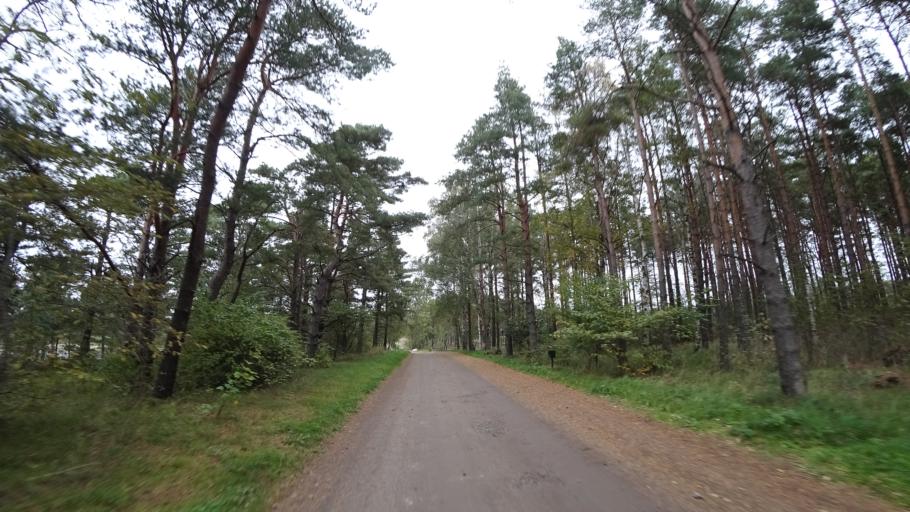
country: SE
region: Skane
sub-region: Kavlinge Kommun
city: Hofterup
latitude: 55.8215
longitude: 12.9512
